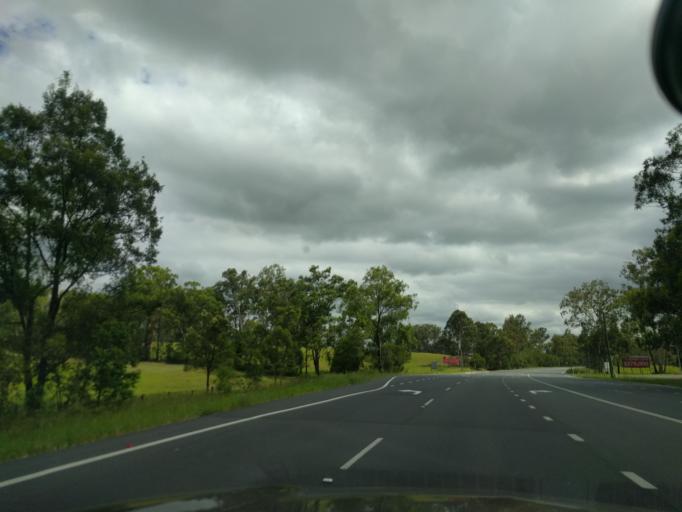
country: AU
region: Queensland
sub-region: Logan
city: Cedar Vale
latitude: -27.8652
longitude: 152.9997
